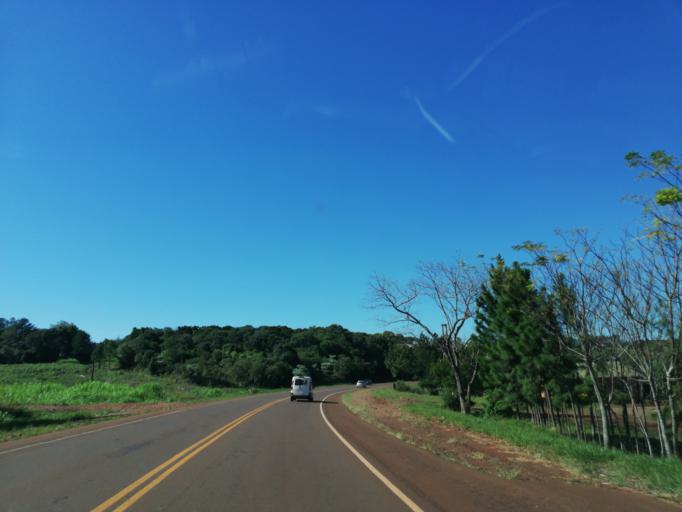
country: AR
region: Misiones
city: Dos de Mayo
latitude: -27.0506
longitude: -54.4315
